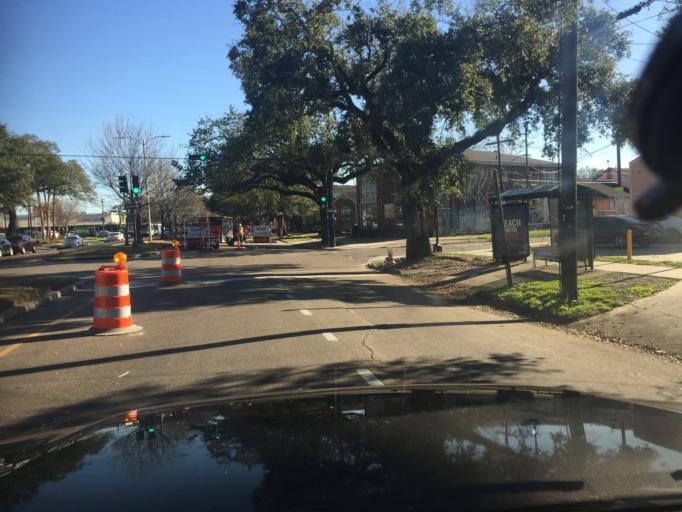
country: US
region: Louisiana
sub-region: Orleans Parish
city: New Orleans
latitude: 29.9787
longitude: -90.0692
